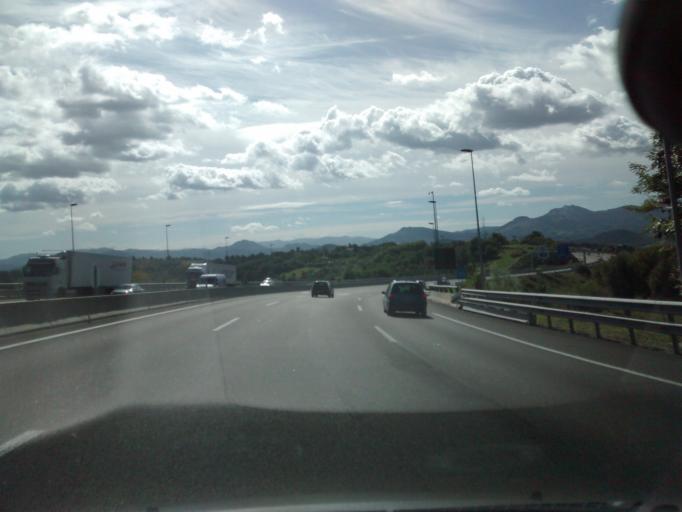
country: ES
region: Basque Country
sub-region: Provincia de Guipuzcoa
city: Usurbil
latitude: 43.2925
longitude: -2.0397
